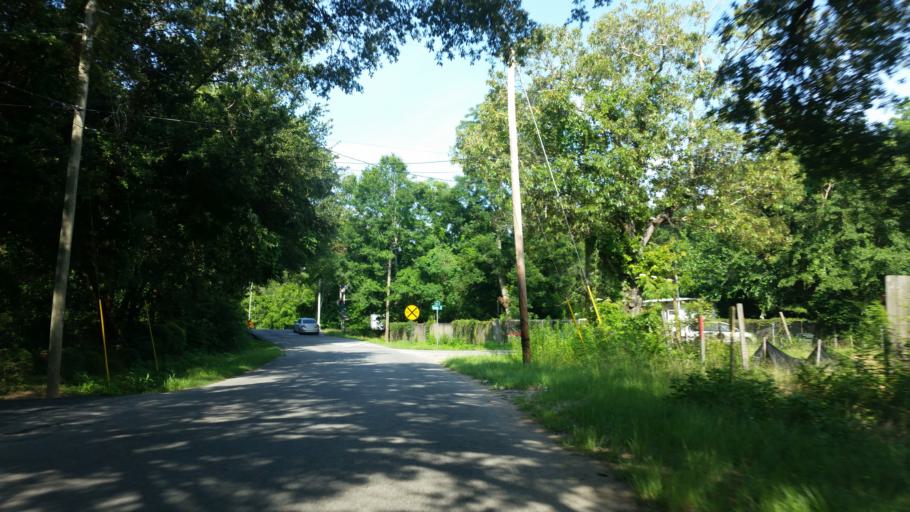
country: US
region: Florida
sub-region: Escambia County
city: Ensley
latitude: 30.5219
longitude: -87.2650
